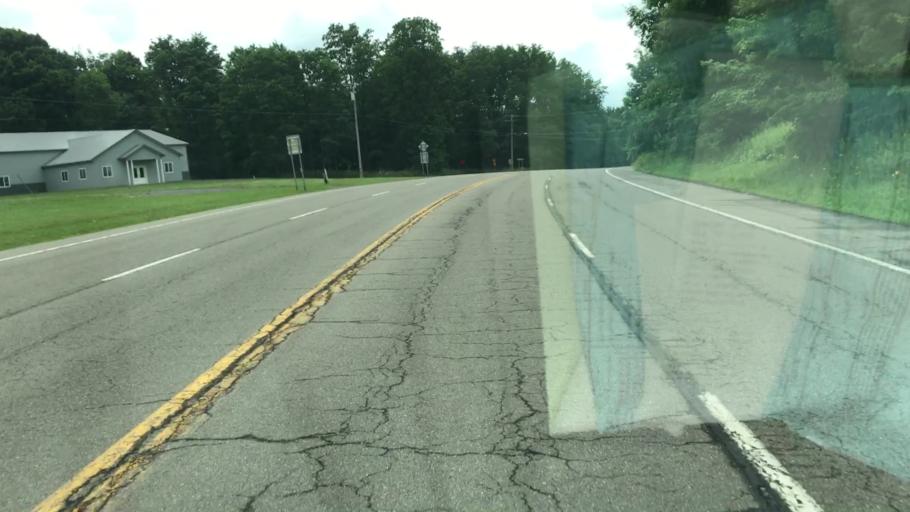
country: US
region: New York
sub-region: Onondaga County
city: Manlius
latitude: 42.9004
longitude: -76.0109
